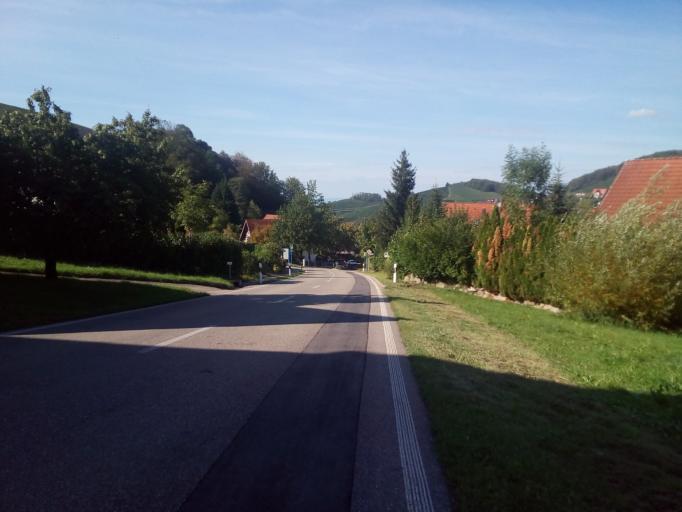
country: DE
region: Baden-Wuerttemberg
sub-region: Freiburg Region
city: Sasbachwalden
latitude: 48.6126
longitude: 8.1300
